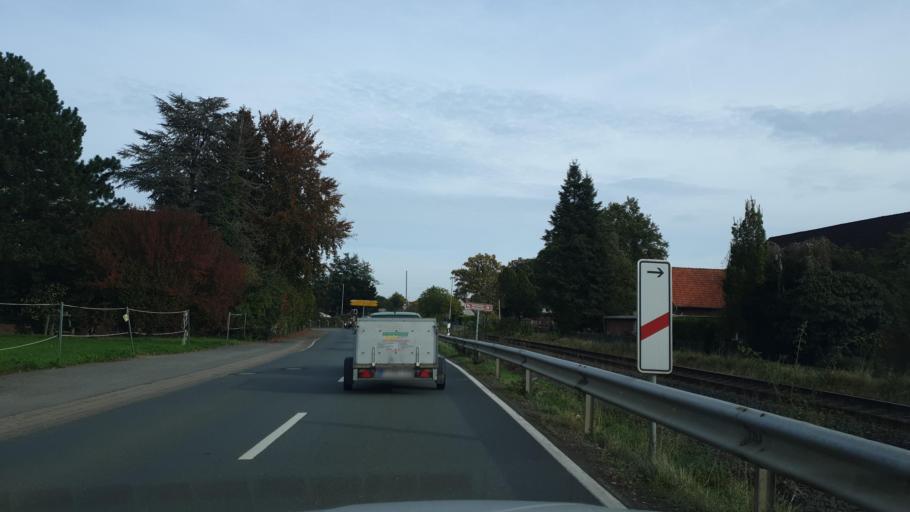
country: DE
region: Lower Saxony
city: Rinteln
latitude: 52.1991
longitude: 9.0135
